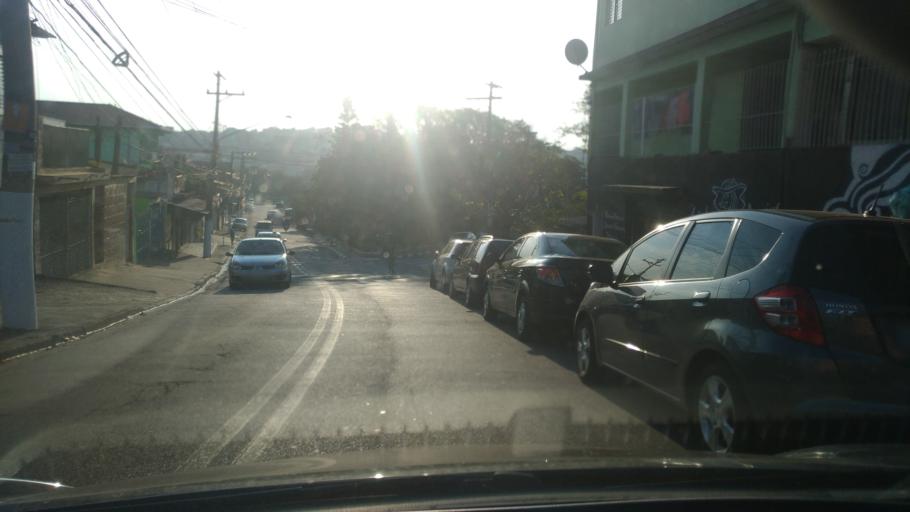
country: BR
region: Sao Paulo
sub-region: Osasco
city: Osasco
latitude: -23.5403
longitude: -46.7964
